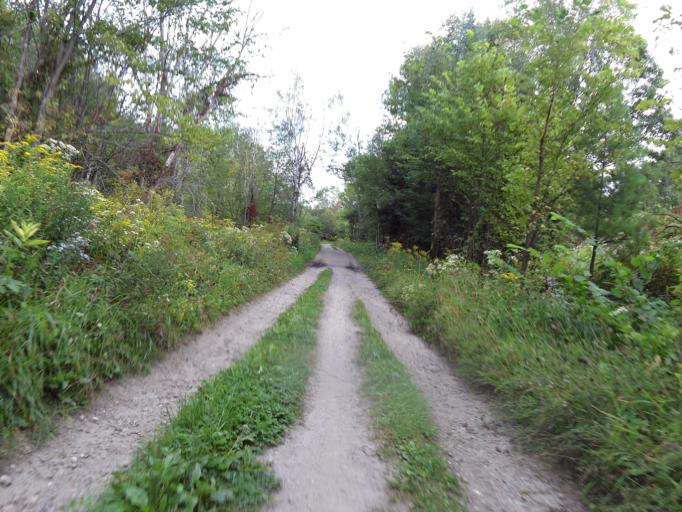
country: CA
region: Quebec
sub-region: Outaouais
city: Wakefield
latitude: 45.6304
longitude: -75.9422
